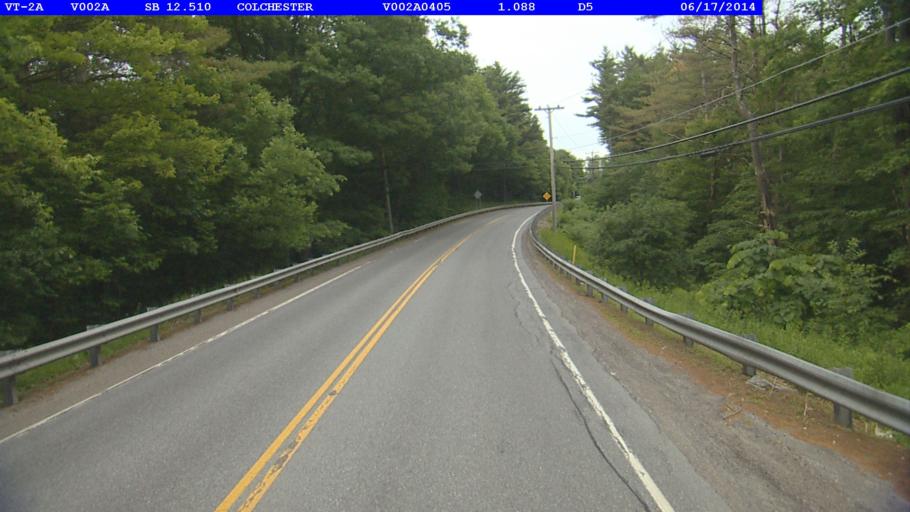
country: US
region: Vermont
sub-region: Chittenden County
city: Colchester
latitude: 44.5400
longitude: -73.1427
